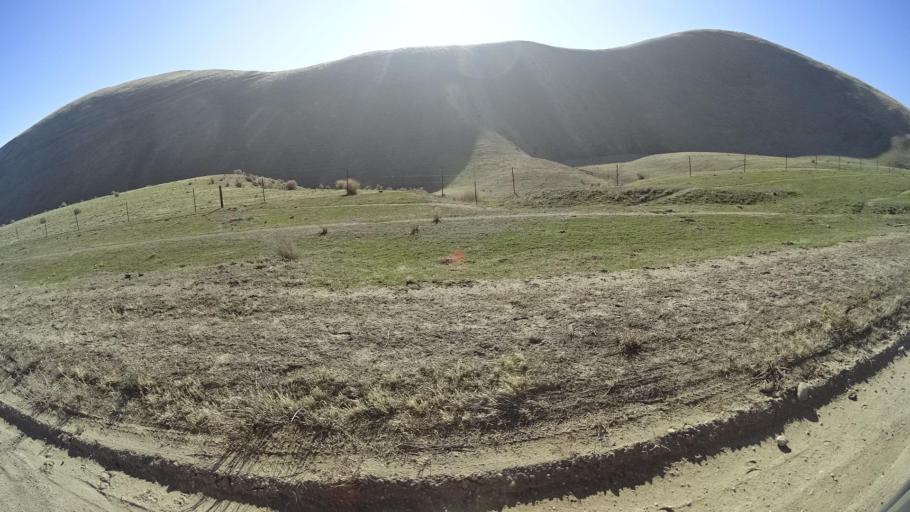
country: US
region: California
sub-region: Kern County
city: Taft Heights
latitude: 35.2297
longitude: -119.6671
